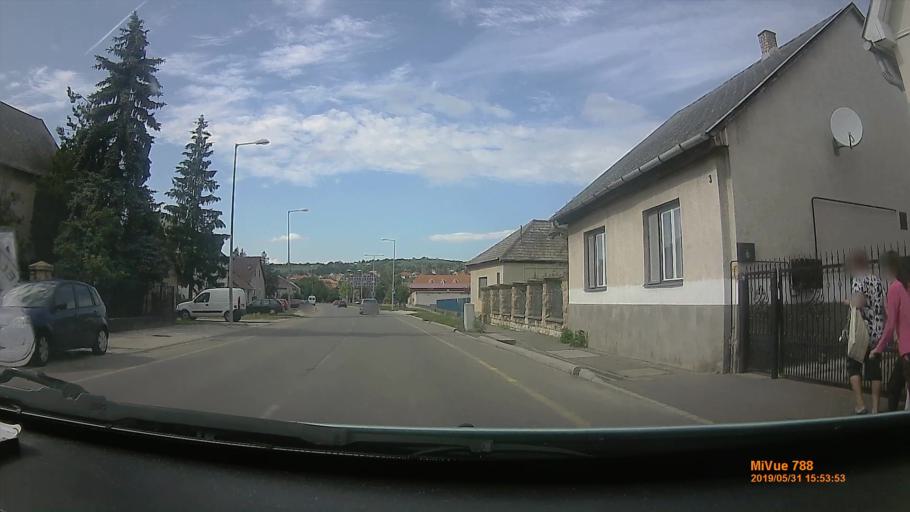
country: HU
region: Borsod-Abauj-Zemplen
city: Szerencs
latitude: 48.1586
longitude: 21.2007
